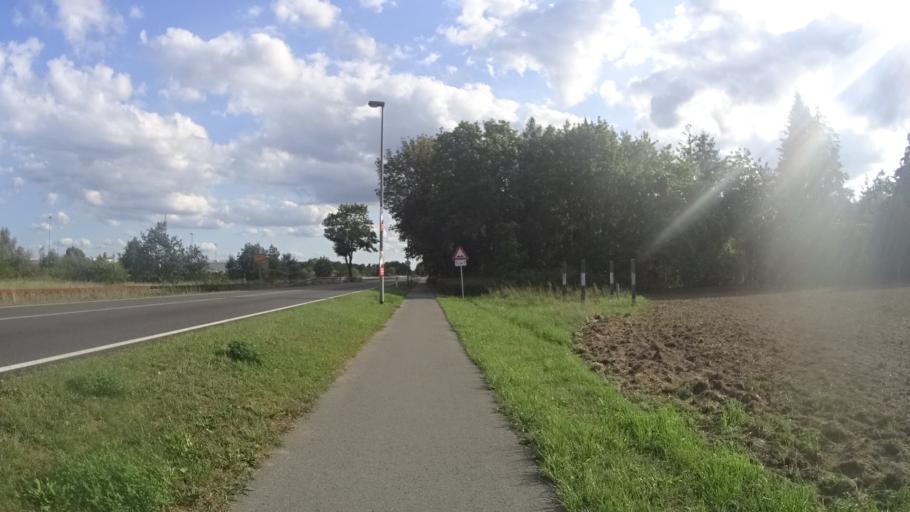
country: DE
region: Brandenburg
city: Rathenow
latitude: 52.5797
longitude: 12.3360
